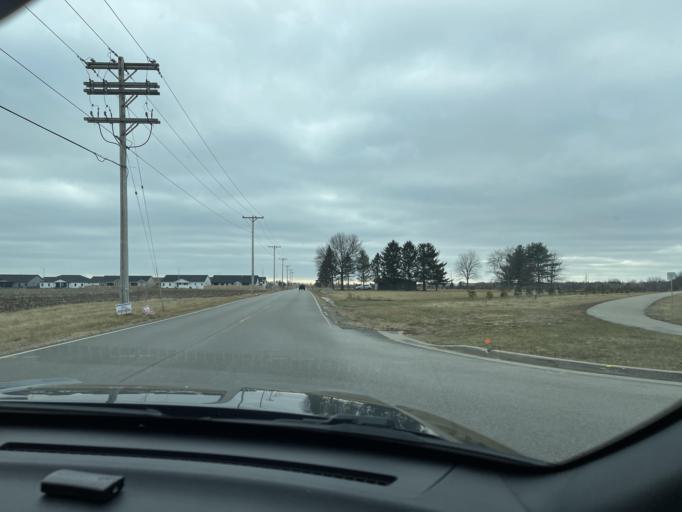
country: US
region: Illinois
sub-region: Sangamon County
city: Jerome
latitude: 39.7652
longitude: -89.7534
